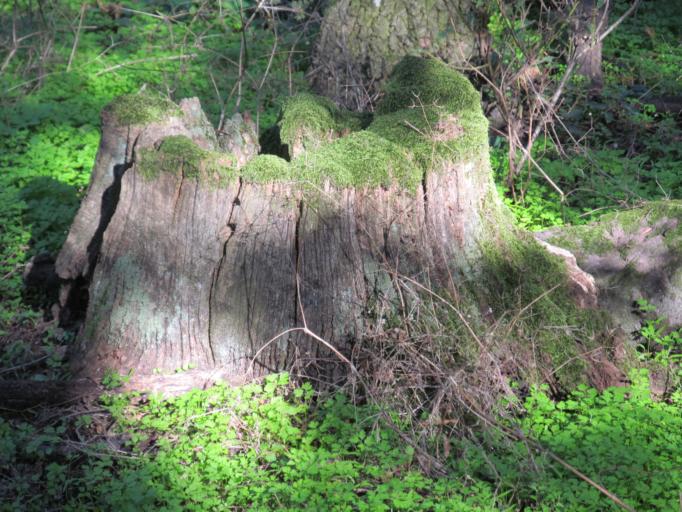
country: HU
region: Pest
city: Szob
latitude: 47.8964
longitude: 18.8229
